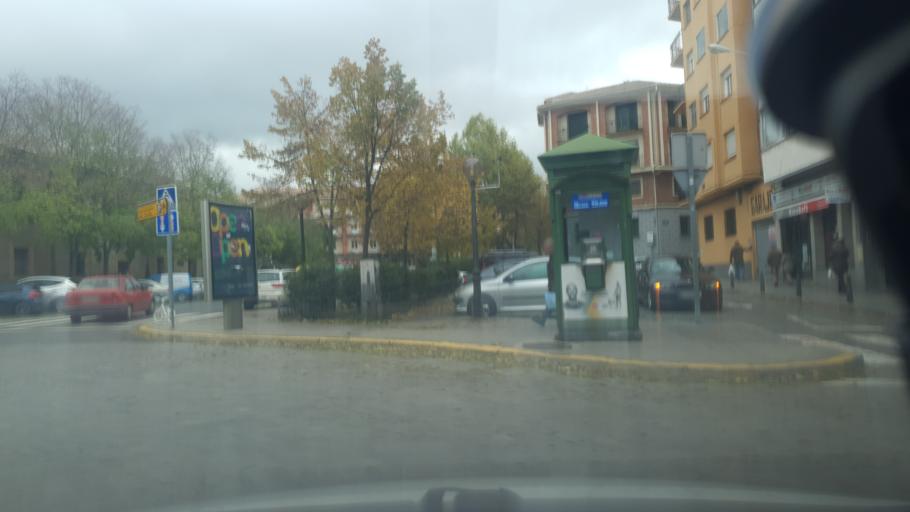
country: ES
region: Castille and Leon
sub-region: Provincia de Segovia
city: Segovia
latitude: 40.9422
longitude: -4.1144
